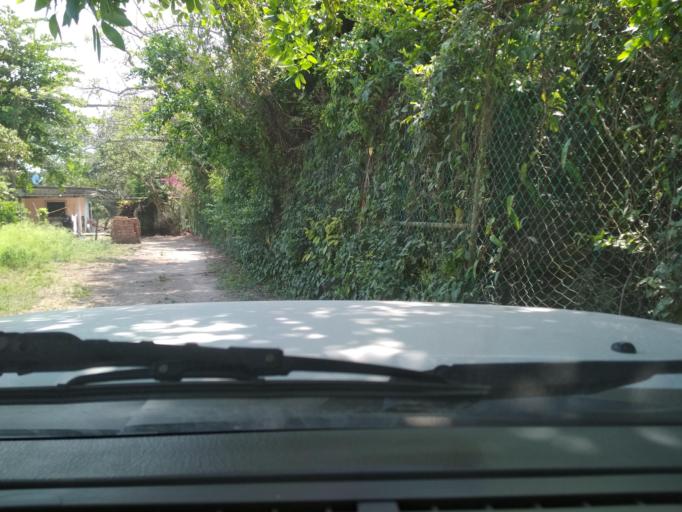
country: MX
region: Veracruz
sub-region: Medellin
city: Fraccionamiento Arboledas San Ramon
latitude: 19.0928
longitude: -96.1445
